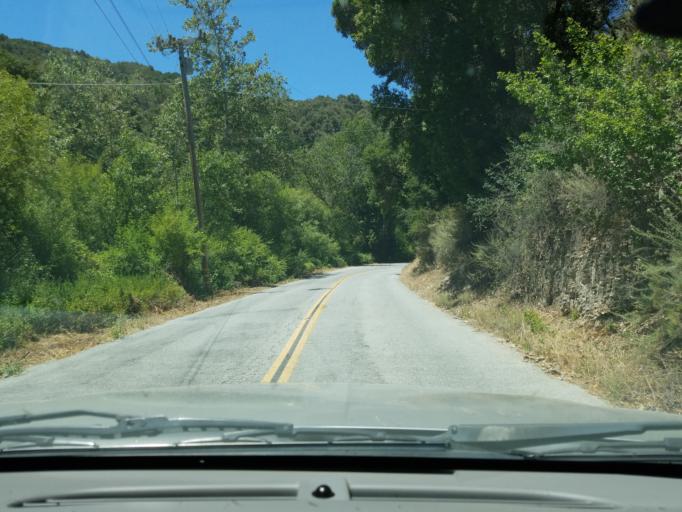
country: US
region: California
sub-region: Monterey County
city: Carmel Valley Village
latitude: 36.4482
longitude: -121.6868
